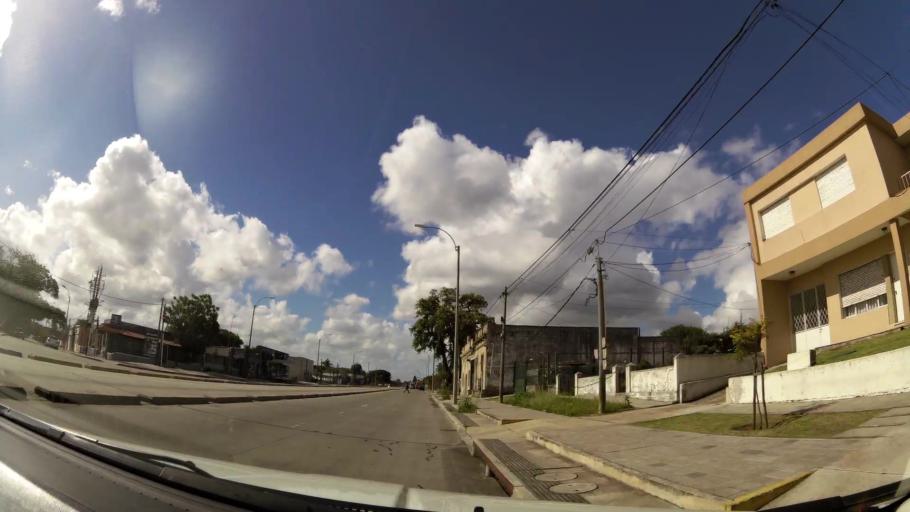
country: UY
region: Canelones
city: La Paz
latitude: -34.8218
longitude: -56.2198
